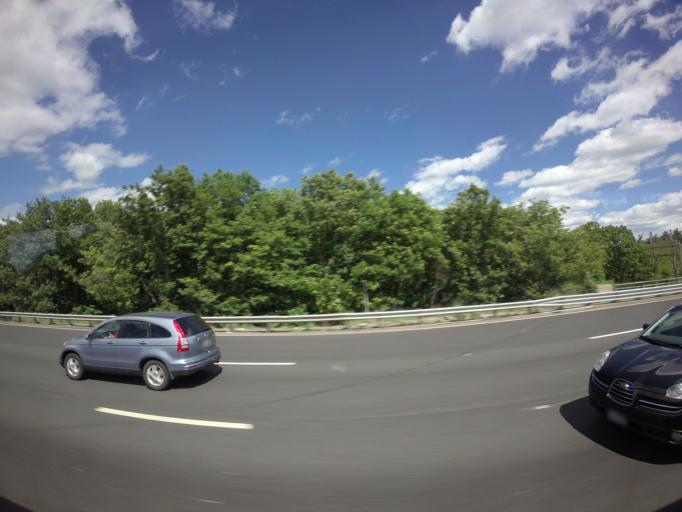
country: US
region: Massachusetts
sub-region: Middlesex County
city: Wilmington
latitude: 42.5413
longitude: -71.1348
